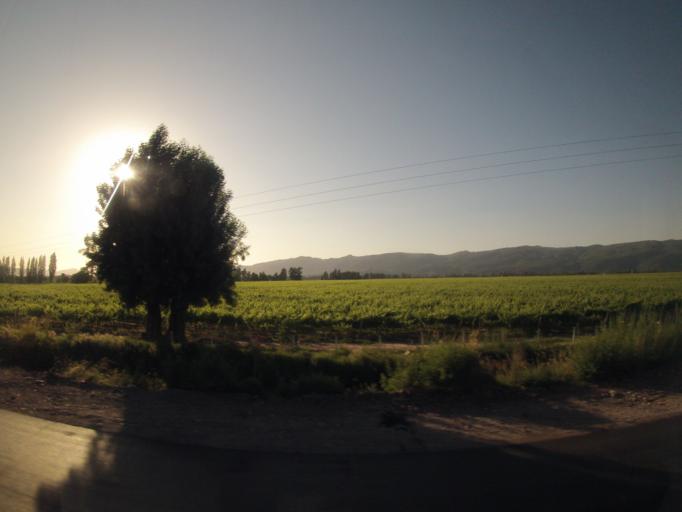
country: CL
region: O'Higgins
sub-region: Provincia de Colchagua
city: Chimbarongo
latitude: -34.7382
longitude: -71.0404
